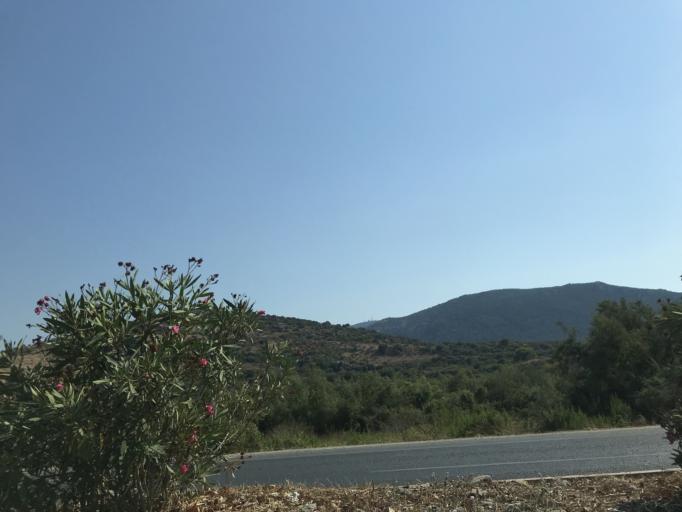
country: TR
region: Izmir
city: Selcuk
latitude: 37.9506
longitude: 27.3481
